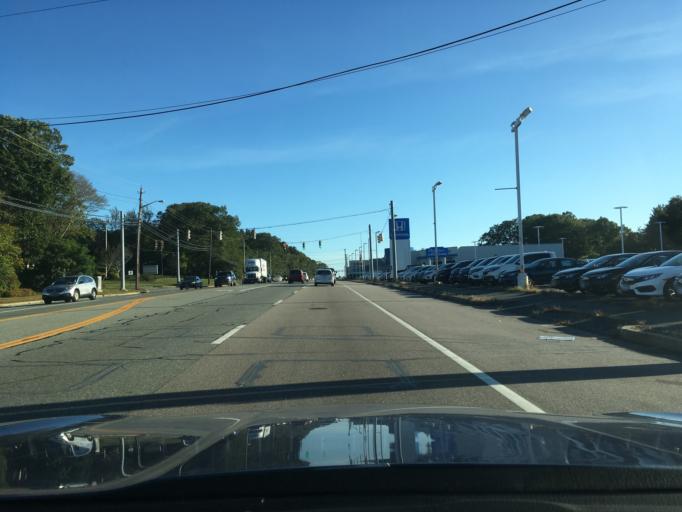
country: US
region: Rhode Island
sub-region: Kent County
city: West Warwick
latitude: 41.6822
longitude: -71.5005
